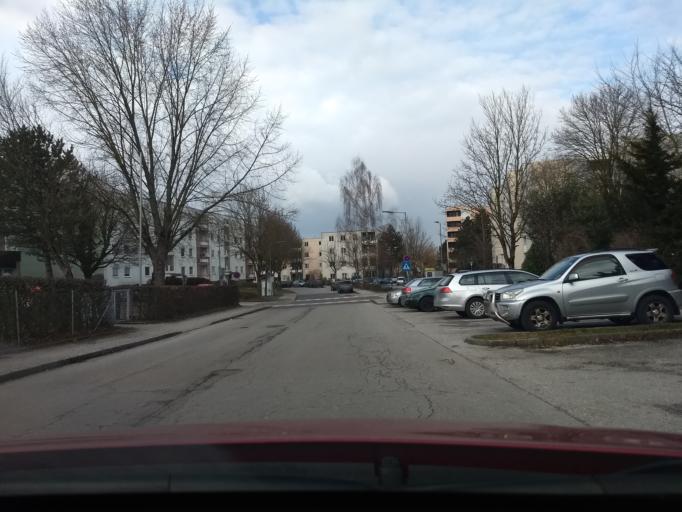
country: AT
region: Upper Austria
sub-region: Steyr Stadt
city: Steyr
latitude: 48.0605
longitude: 14.4239
